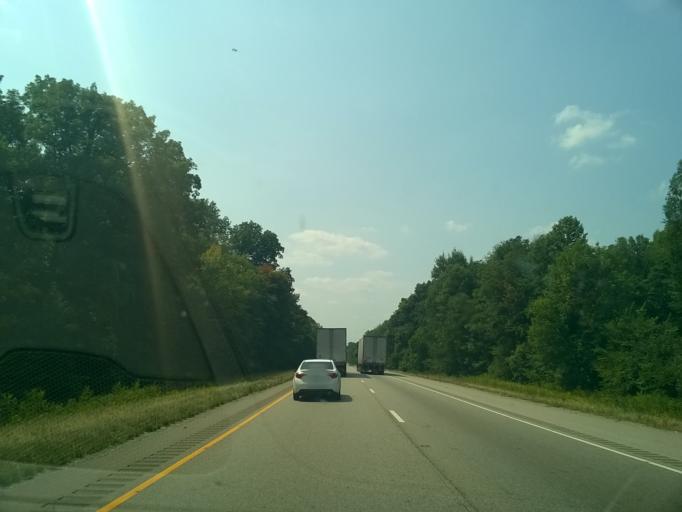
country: US
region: Indiana
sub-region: Vigo County
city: Seelyville
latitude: 39.4449
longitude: -87.2627
